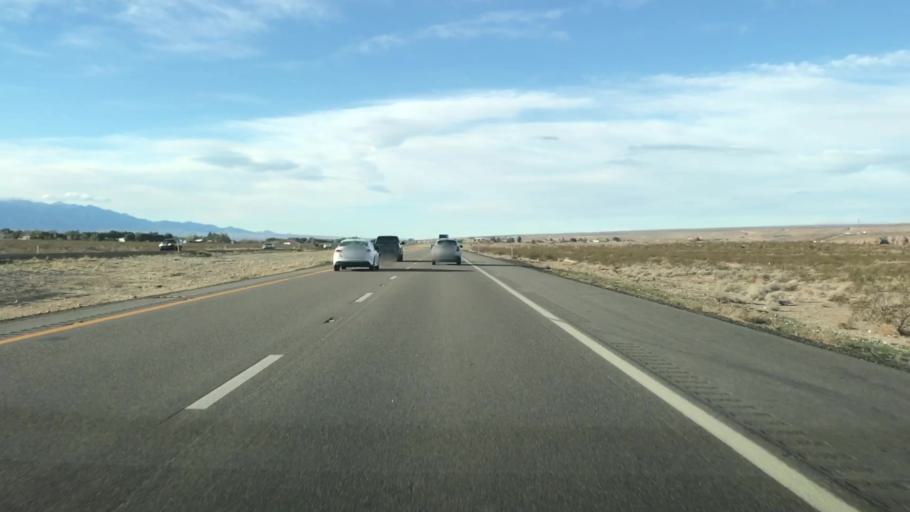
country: US
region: Arizona
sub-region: Mohave County
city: Beaver Dam
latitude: 36.9089
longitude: -113.8909
